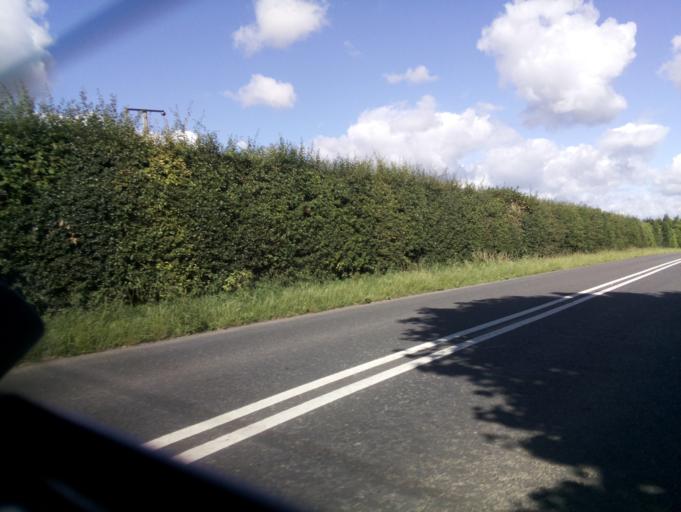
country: GB
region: England
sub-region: Gloucestershire
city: Newent
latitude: 51.9186
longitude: -2.3511
